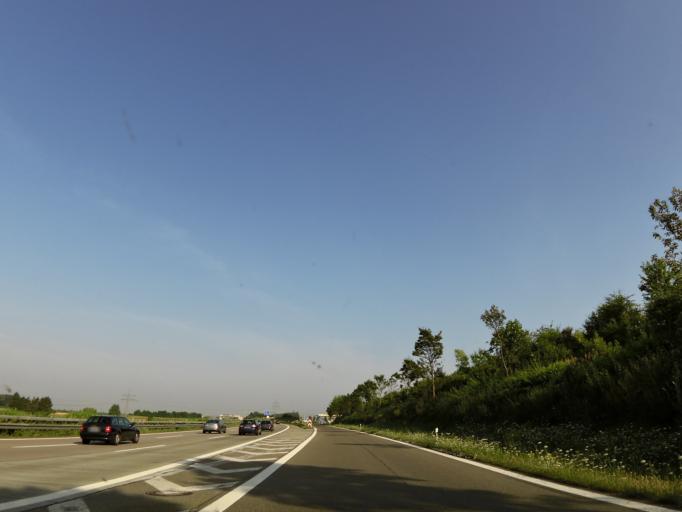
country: DE
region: Baden-Wuerttemberg
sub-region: Regierungsbezirk Stuttgart
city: Denkendorf
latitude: 48.6913
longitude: 9.3095
